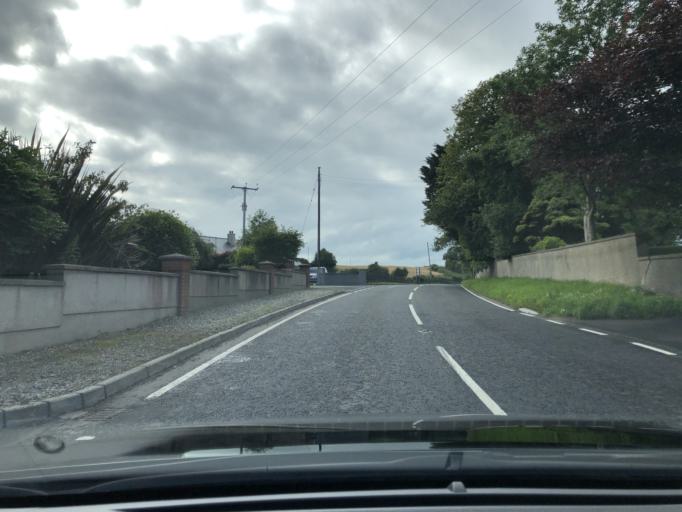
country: GB
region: Northern Ireland
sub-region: Down District
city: Dundrum
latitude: 54.2860
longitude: -5.8263
